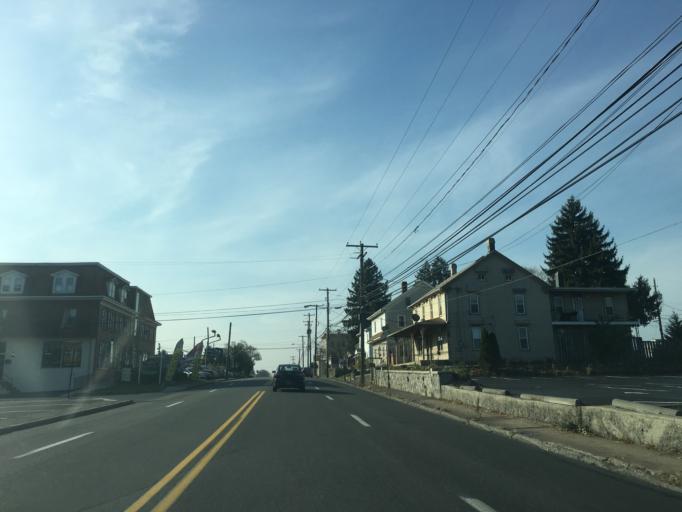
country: US
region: Pennsylvania
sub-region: Dauphin County
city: Progress
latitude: 40.2878
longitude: -76.8379
